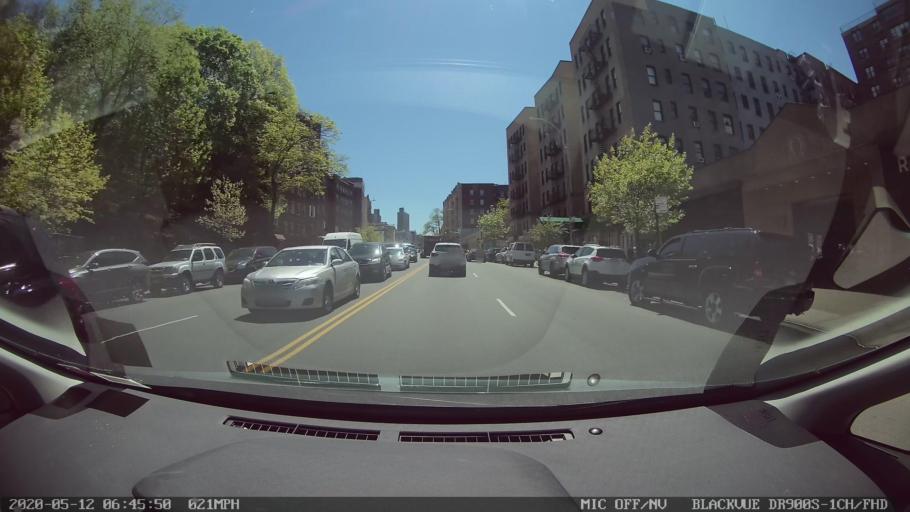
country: US
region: New York
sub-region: New York County
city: Inwood
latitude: 40.8560
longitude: -73.9330
